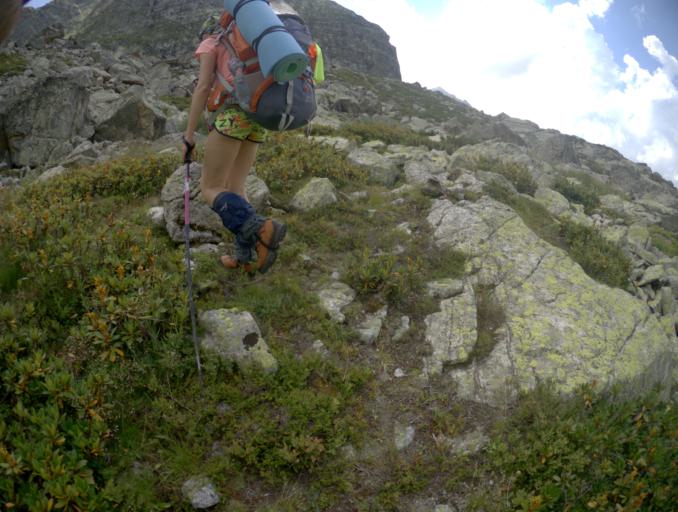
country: RU
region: Karachayevo-Cherkesiya
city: Uchkulan
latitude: 43.2884
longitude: 42.0811
